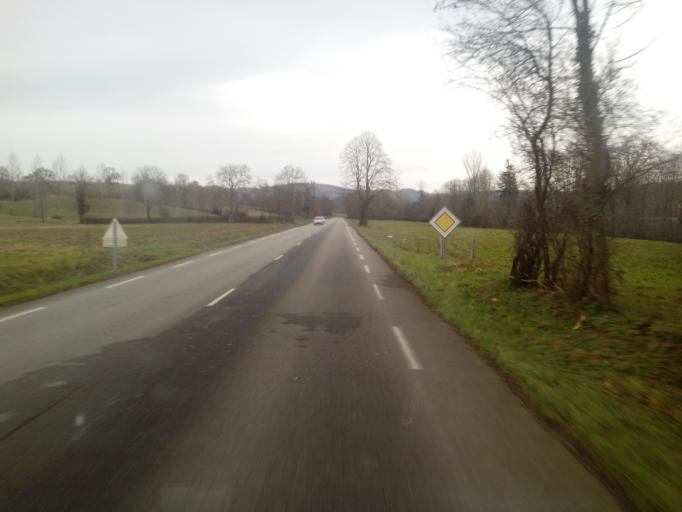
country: FR
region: Midi-Pyrenees
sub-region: Departement de l'Ariege
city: Montjoie-en-Couserans
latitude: 43.0022
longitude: 1.3508
